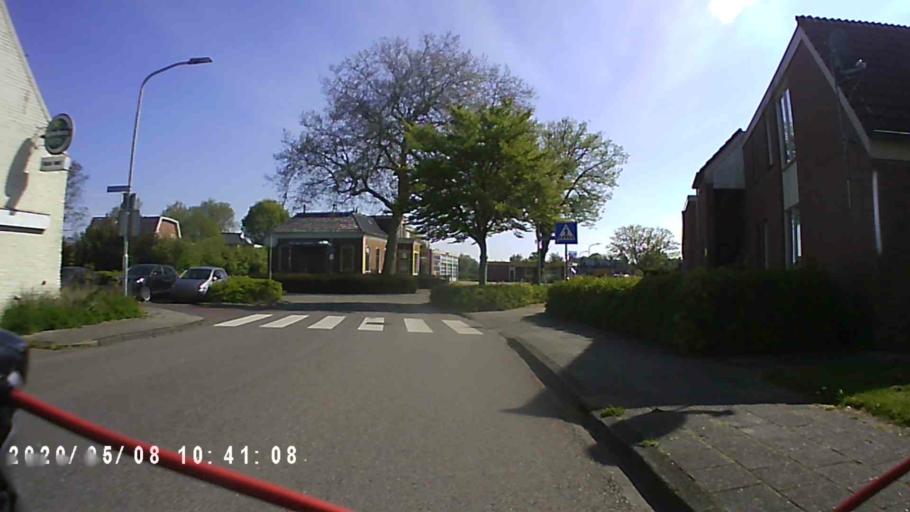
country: NL
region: Groningen
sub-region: Gemeente Winsum
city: Winsum
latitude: 53.3314
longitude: 6.5178
